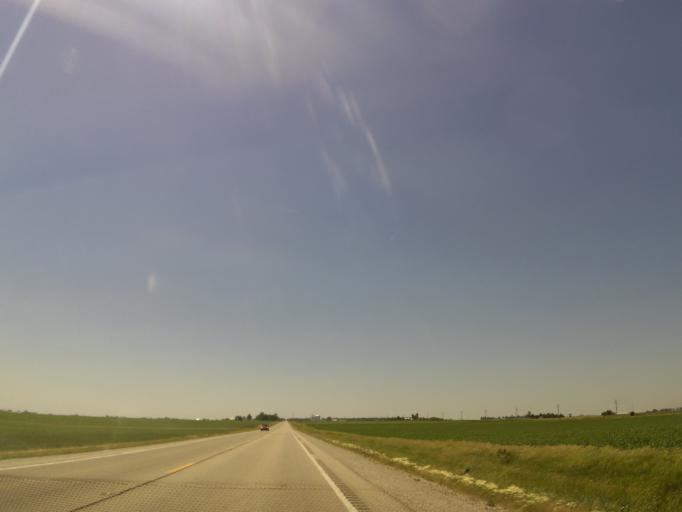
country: US
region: Illinois
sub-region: McLean County
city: Gridley
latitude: 40.7403
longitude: -88.8375
